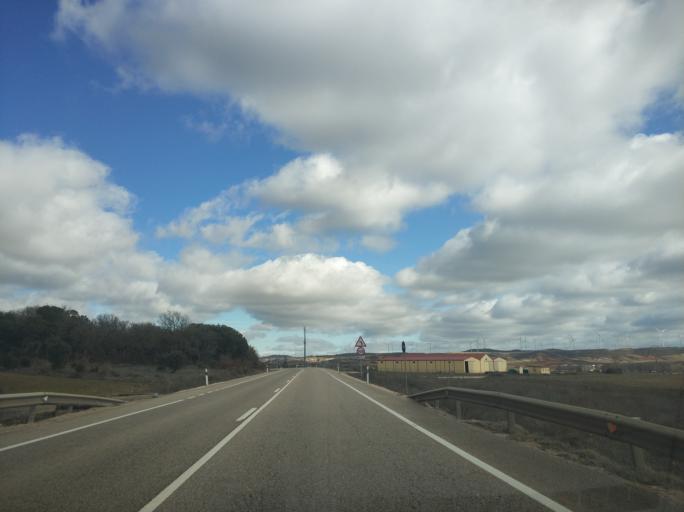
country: ES
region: Castille and Leon
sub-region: Provincia de Burgos
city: Revillarruz
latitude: 42.2173
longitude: -3.6528
